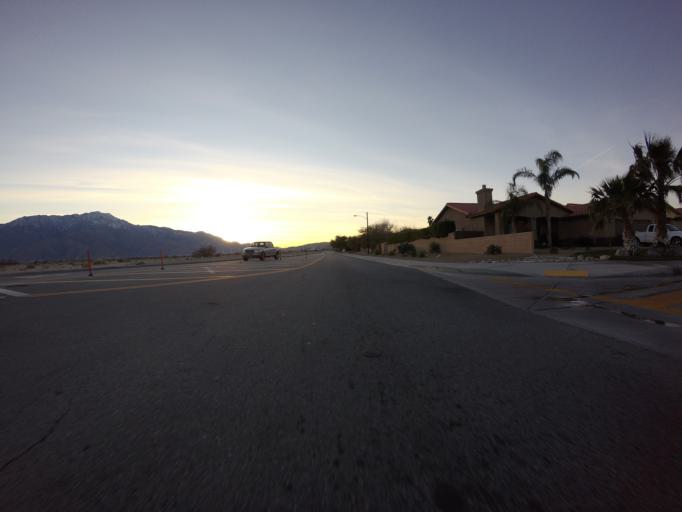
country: US
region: California
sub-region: Riverside County
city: Desert Hot Springs
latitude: 33.9468
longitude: -116.5101
